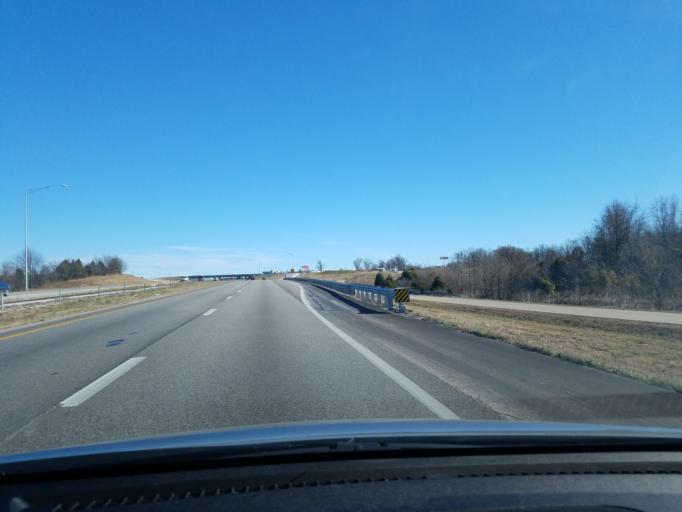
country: US
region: Missouri
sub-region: Greene County
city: Strafford
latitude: 37.2501
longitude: -93.1897
